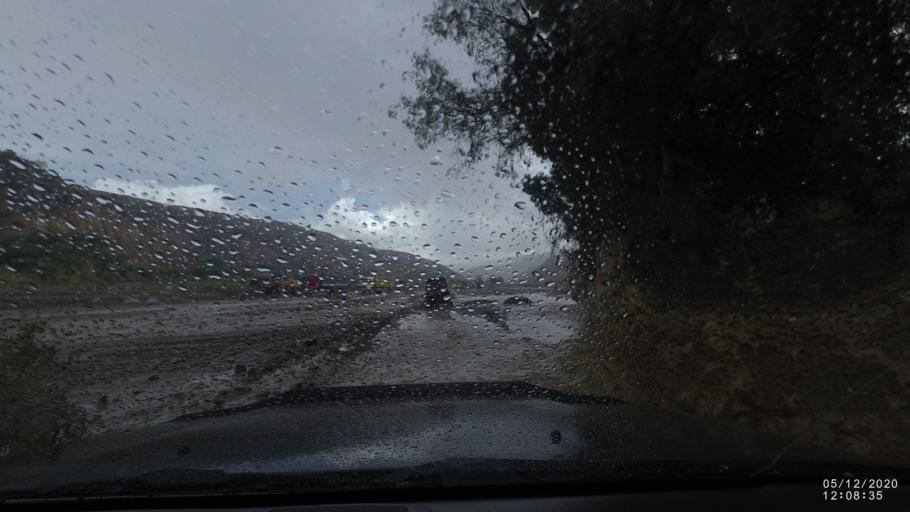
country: BO
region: Cochabamba
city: Sipe Sipe
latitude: -17.5706
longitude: -66.3677
